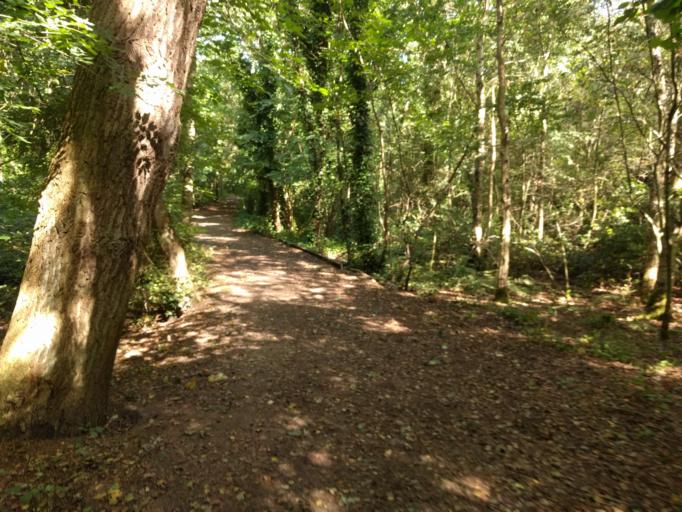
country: GB
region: England
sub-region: Warrington
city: Culcheth
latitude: 53.4241
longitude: -2.5047
